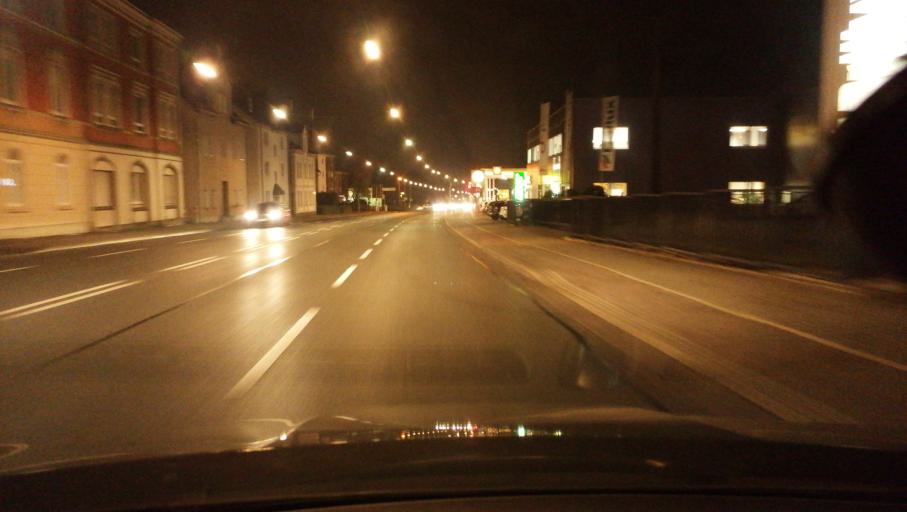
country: DE
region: North Rhine-Westphalia
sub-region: Regierungsbezirk Munster
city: Recklinghausen
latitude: 51.6096
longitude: 7.1833
